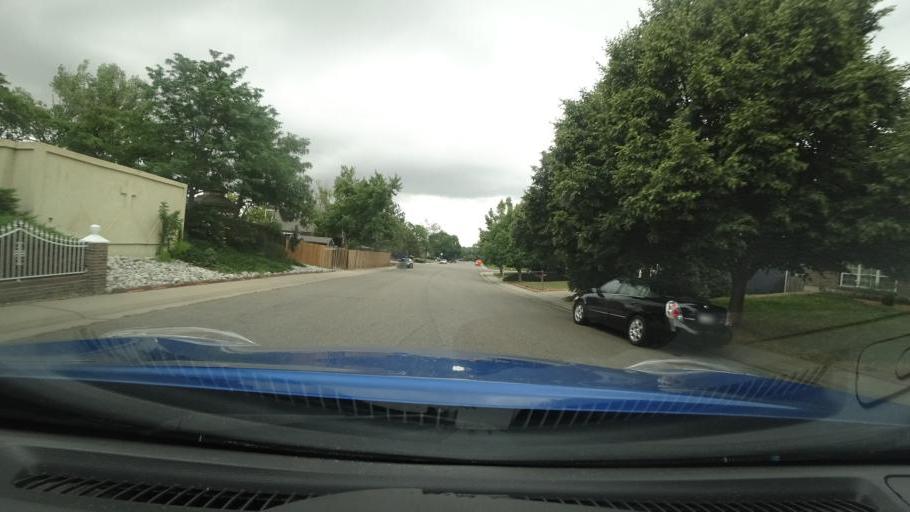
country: US
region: Colorado
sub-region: Adams County
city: Aurora
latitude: 39.7009
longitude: -104.8126
